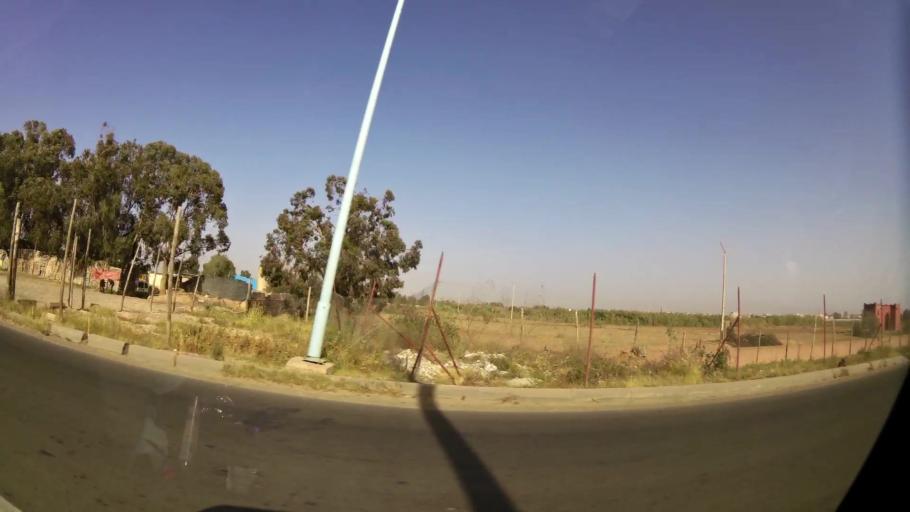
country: MA
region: Souss-Massa-Draa
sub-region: Inezgane-Ait Mellou
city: Inezgane
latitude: 30.3604
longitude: -9.5060
